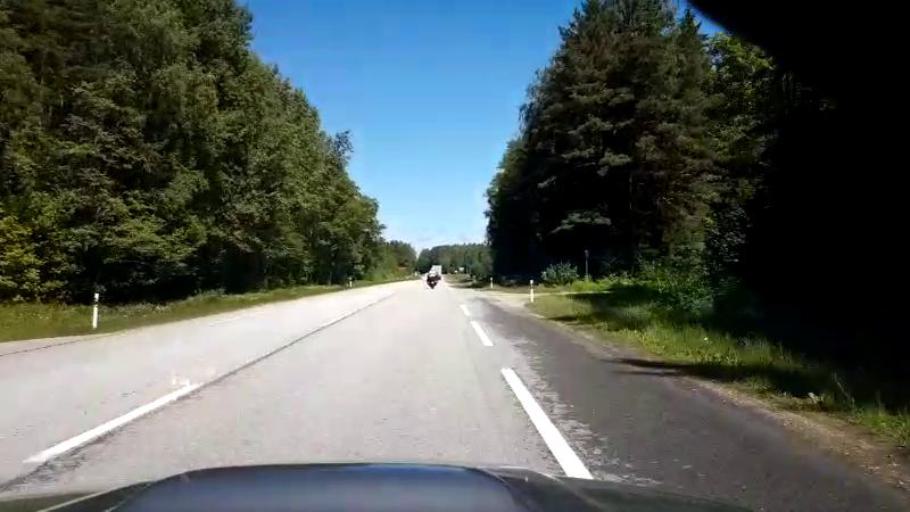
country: LV
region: Saulkrastu
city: Saulkrasti
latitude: 57.4335
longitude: 24.4298
